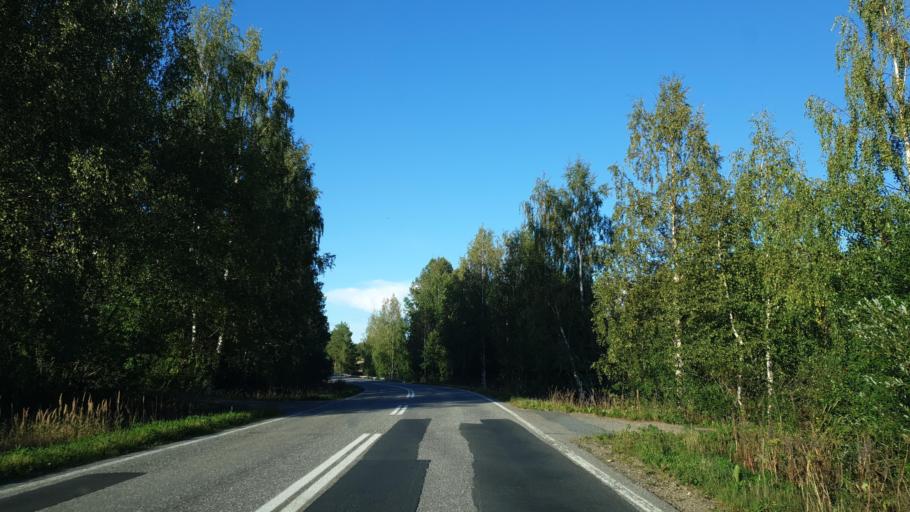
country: FI
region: Northern Savo
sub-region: Koillis-Savo
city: Juankoski
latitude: 63.1115
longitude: 28.4460
